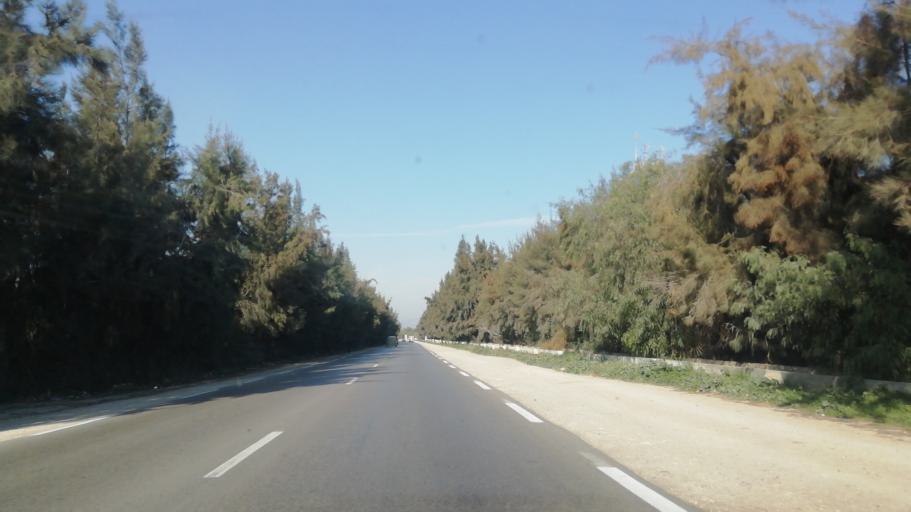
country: DZ
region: Relizane
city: Relizane
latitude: 35.7304
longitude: 0.4734
